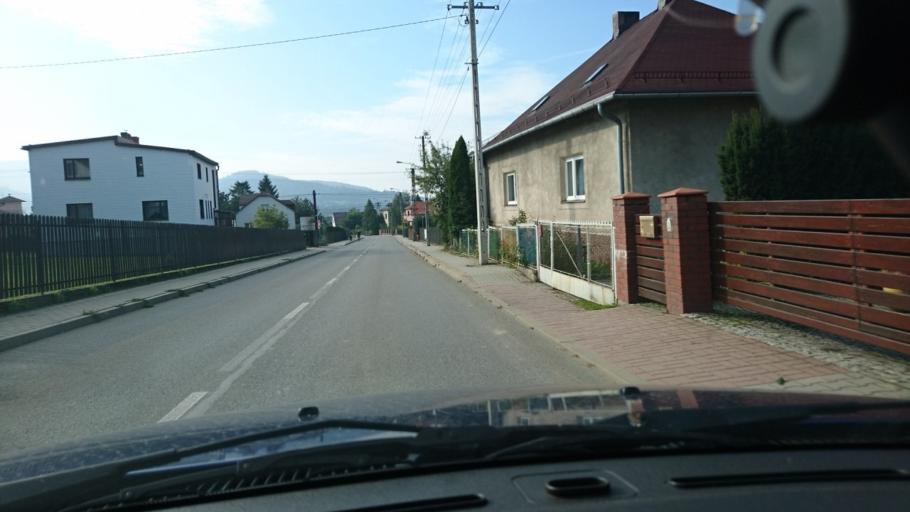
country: PL
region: Silesian Voivodeship
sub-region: Powiat bielski
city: Wilkowice
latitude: 49.7608
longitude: 19.0981
